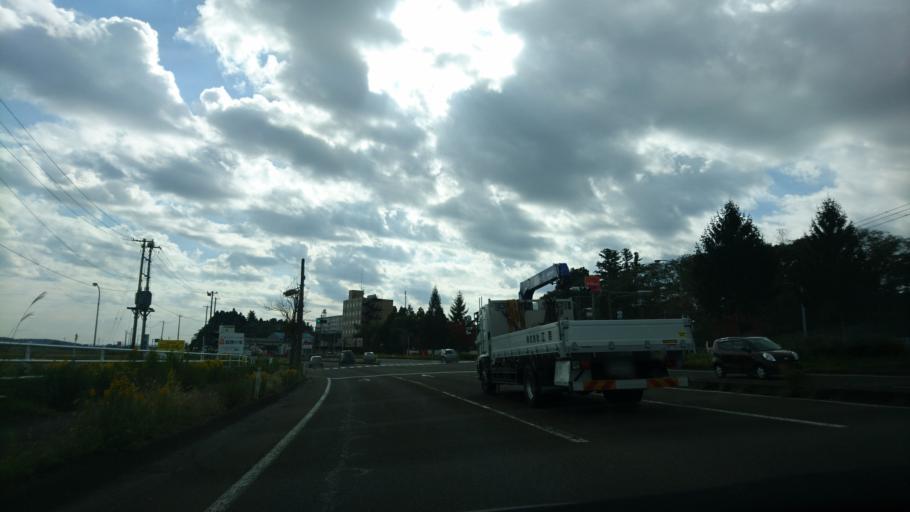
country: JP
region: Miyagi
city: Tomiya
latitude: 38.4539
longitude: 140.8800
